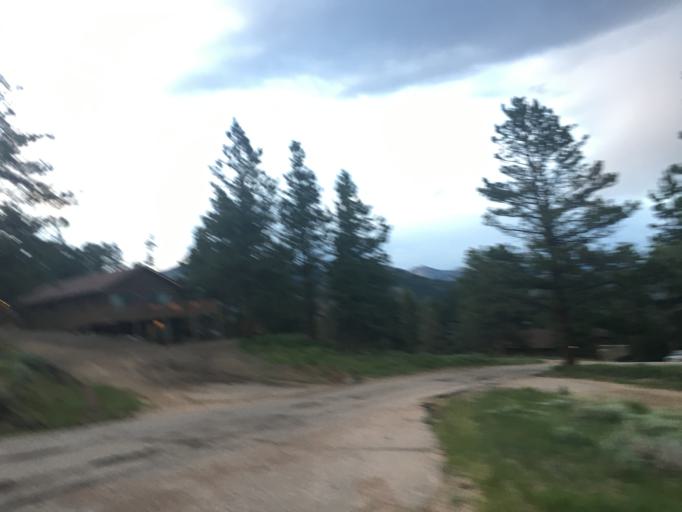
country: US
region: Colorado
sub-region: Larimer County
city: Estes Park
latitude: 40.3372
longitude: -105.5810
